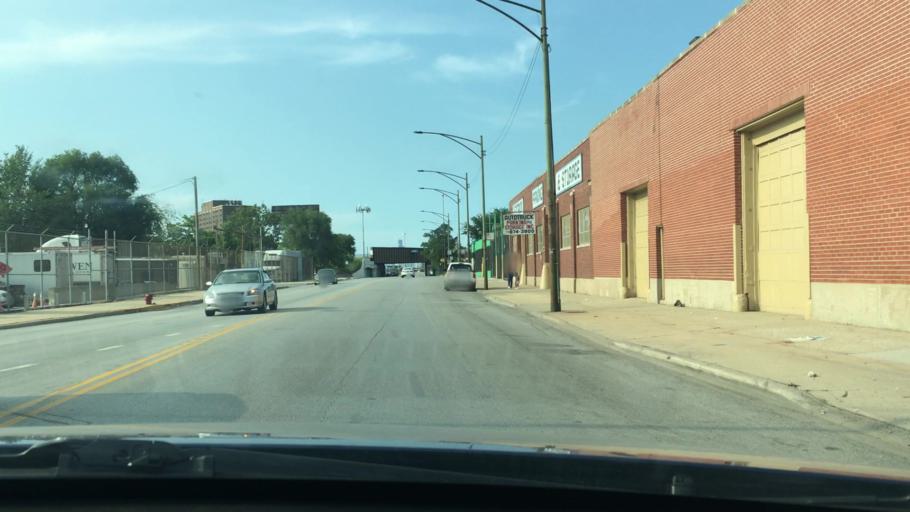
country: US
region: Illinois
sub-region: Cook County
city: Chicago
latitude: 41.7733
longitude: -87.6300
